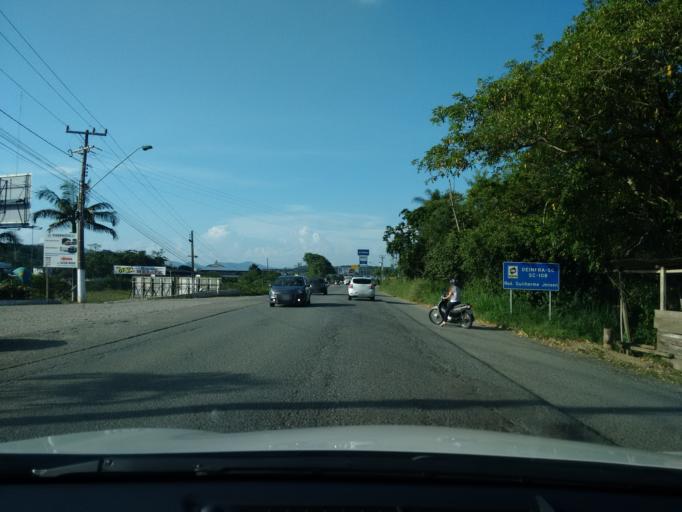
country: BR
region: Santa Catarina
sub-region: Blumenau
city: Blumenau
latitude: -26.8592
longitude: -49.0860
